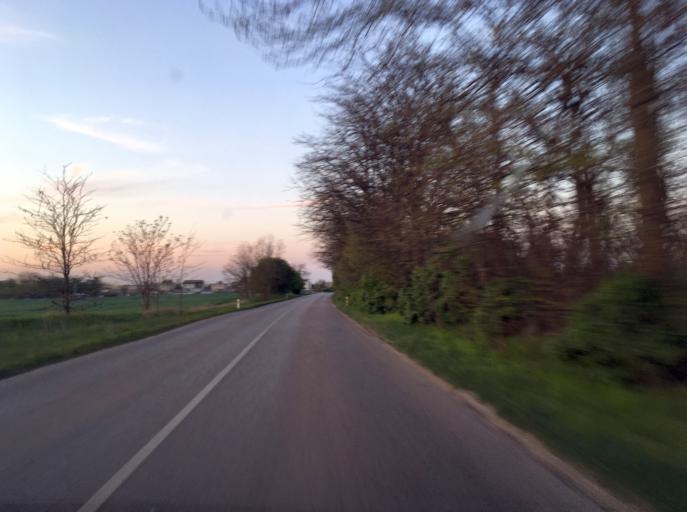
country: SK
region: Nitriansky
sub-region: Okres Nove Zamky
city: Nove Zamky
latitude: 47.9525
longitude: 18.1393
